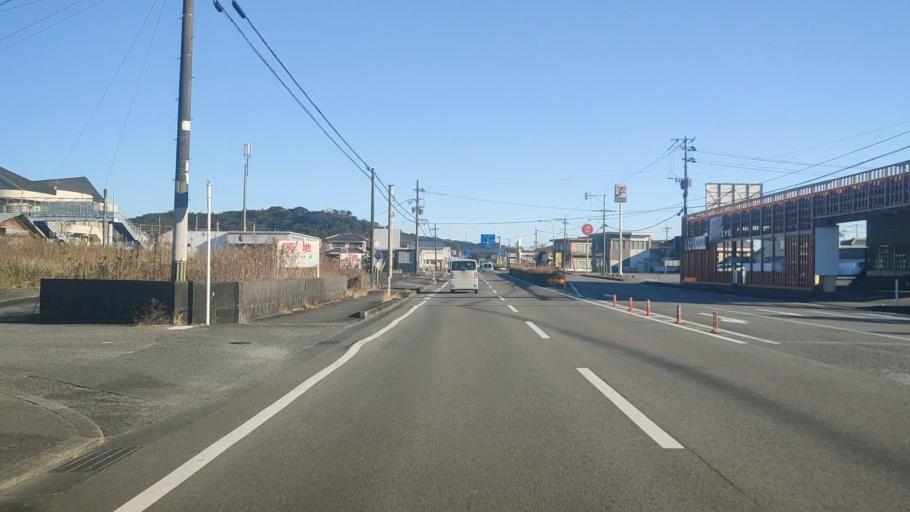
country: JP
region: Miyazaki
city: Nobeoka
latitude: 32.4759
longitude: 131.6537
